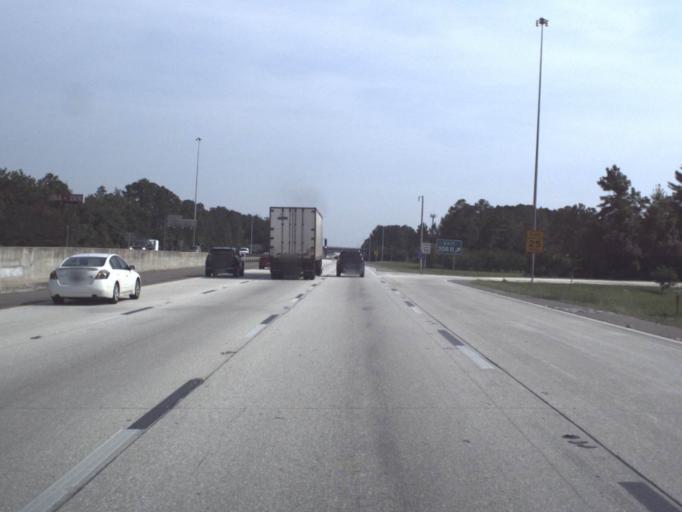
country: US
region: Florida
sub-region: Duval County
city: Jacksonville
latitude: 30.4086
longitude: -81.6573
